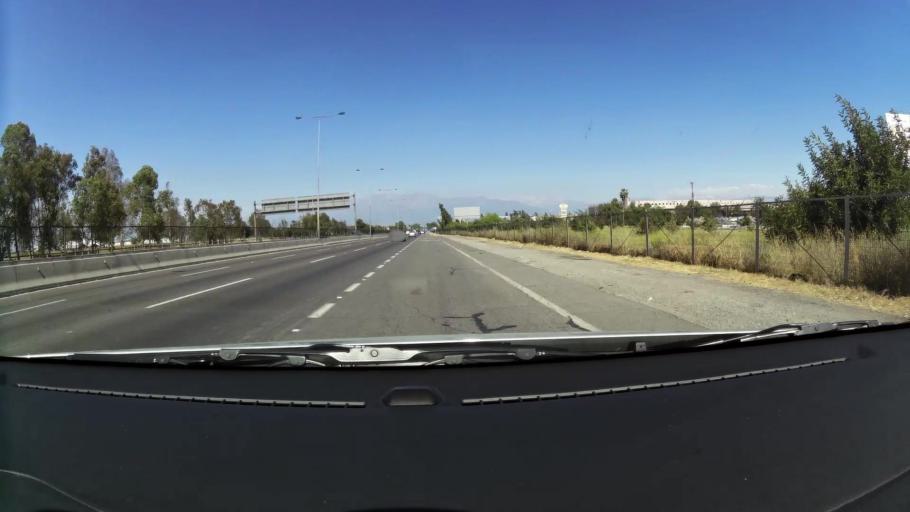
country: CL
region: Santiago Metropolitan
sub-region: Provincia de Santiago
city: Lo Prado
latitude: -33.4468
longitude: -70.7745
